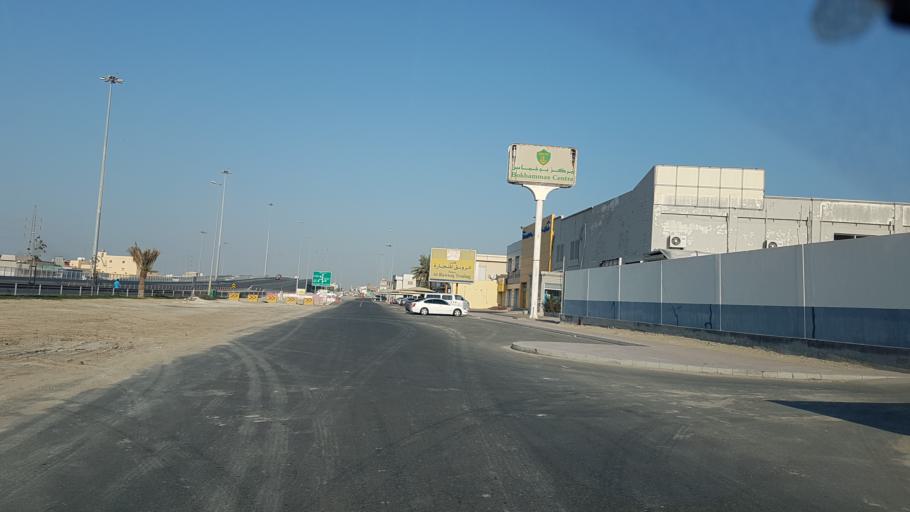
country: BH
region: Northern
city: Sitrah
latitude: 26.1277
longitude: 50.5979
